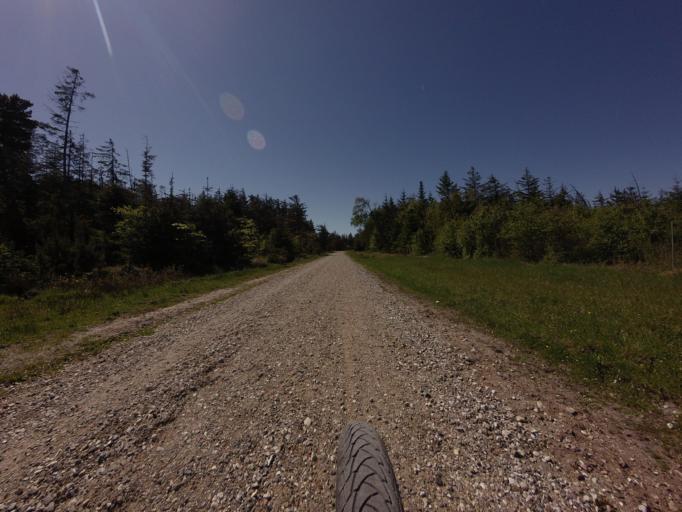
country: DK
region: North Denmark
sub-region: Jammerbugt Kommune
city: Pandrup
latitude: 57.2405
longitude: 9.5849
